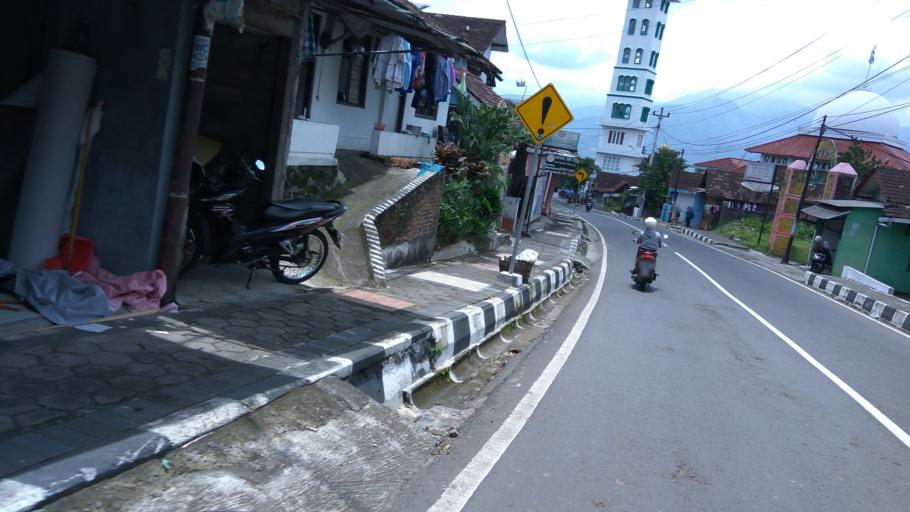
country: ID
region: Central Java
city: Ambarawa
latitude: -7.2549
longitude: 110.4031
